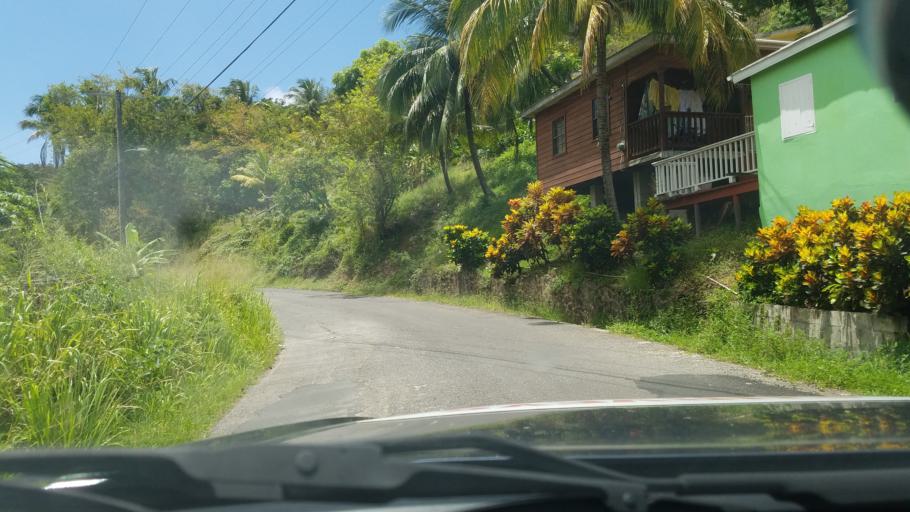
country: LC
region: Gros-Islet
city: Gros Islet
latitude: 14.0562
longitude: -60.9362
